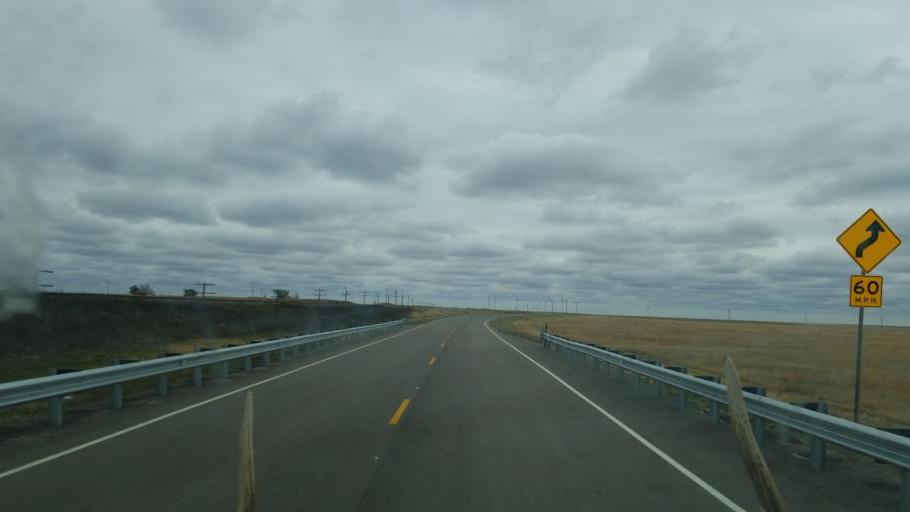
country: US
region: Colorado
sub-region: Kiowa County
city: Eads
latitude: 38.5035
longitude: -103.0303
